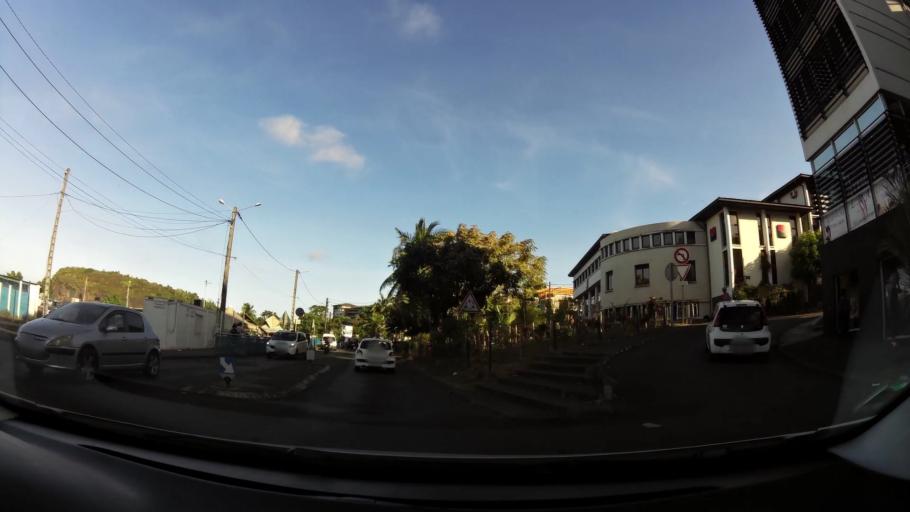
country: YT
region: Mamoudzou
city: Mamoudzou
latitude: -12.7774
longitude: 45.2318
